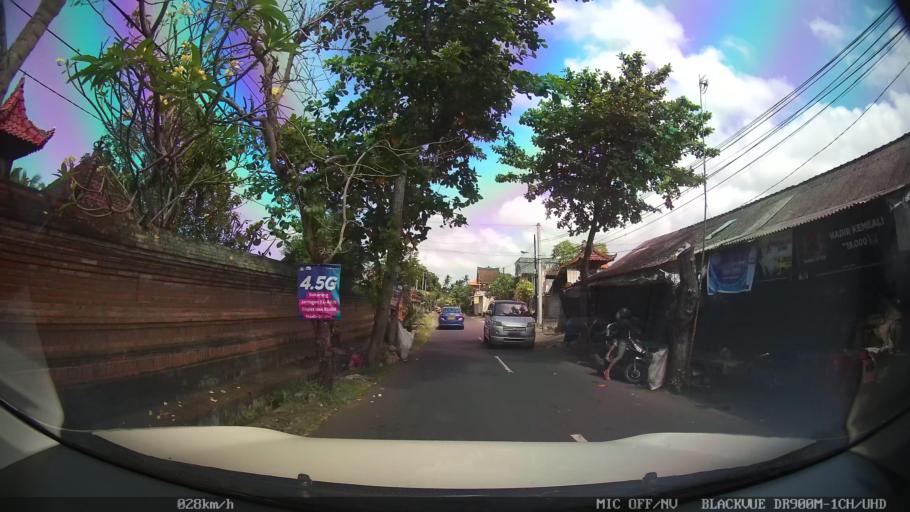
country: ID
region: Bali
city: Banjar Pasekan
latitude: -8.6025
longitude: 115.3106
